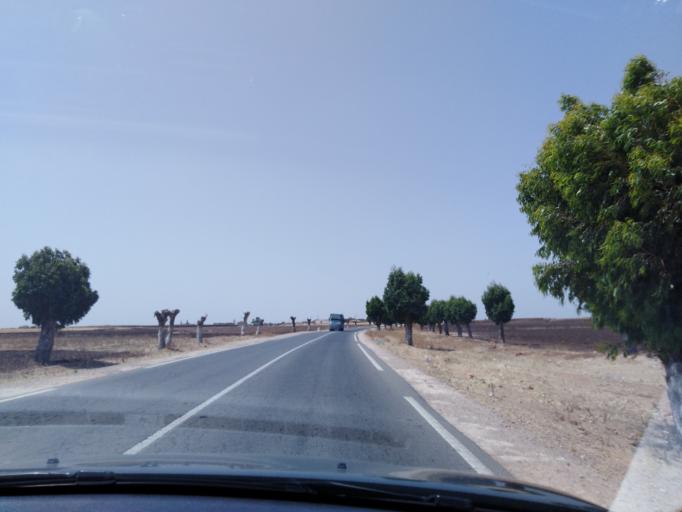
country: MA
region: Doukkala-Abda
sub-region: Safi
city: Youssoufia
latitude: 32.3798
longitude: -8.8266
